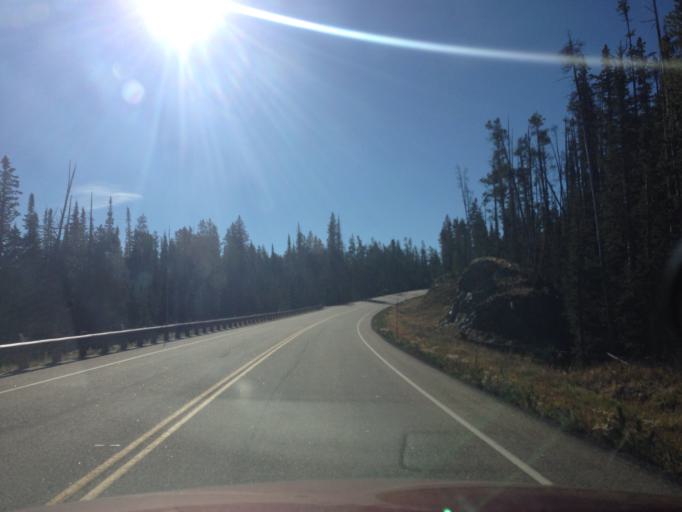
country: US
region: Montana
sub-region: Carbon County
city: Red Lodge
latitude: 45.0177
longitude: -109.8718
